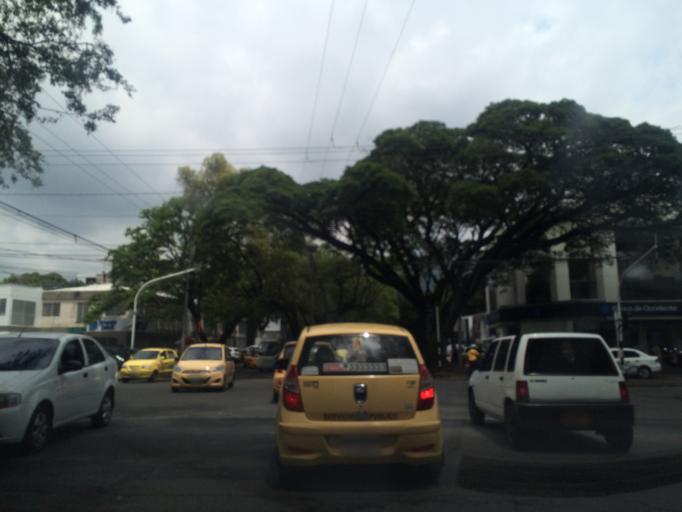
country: CO
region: Valle del Cauca
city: Cali
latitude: 3.4200
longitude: -76.5425
